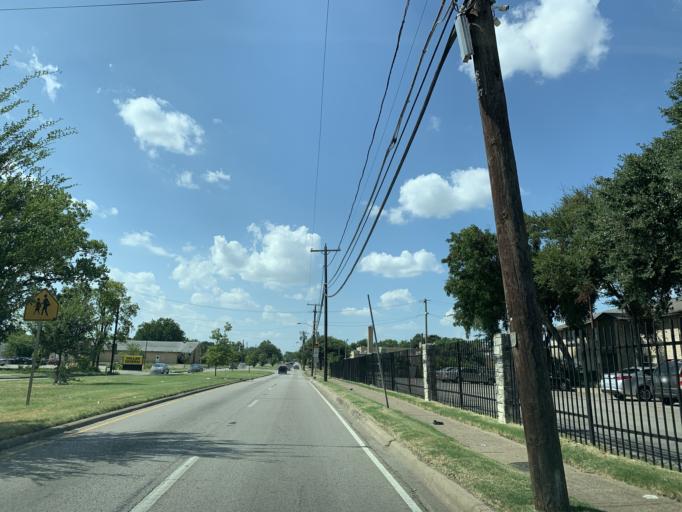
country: US
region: Texas
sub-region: Dallas County
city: Hutchins
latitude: 32.6962
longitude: -96.7731
